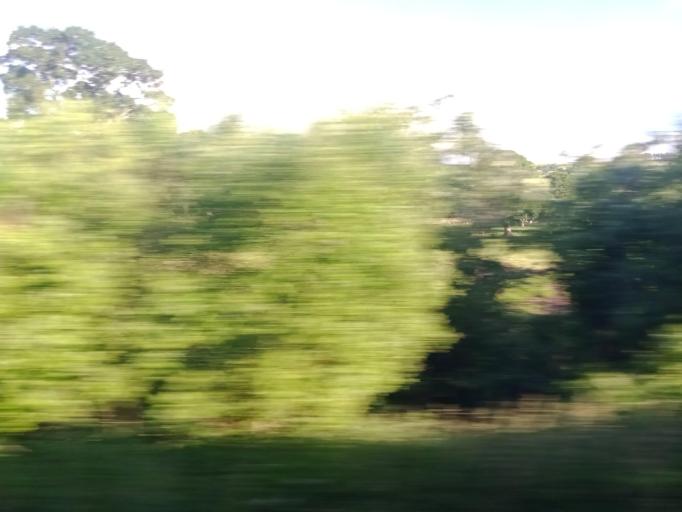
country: GB
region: Wales
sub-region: Gwynedd
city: Aber
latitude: 53.2304
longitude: -4.0481
